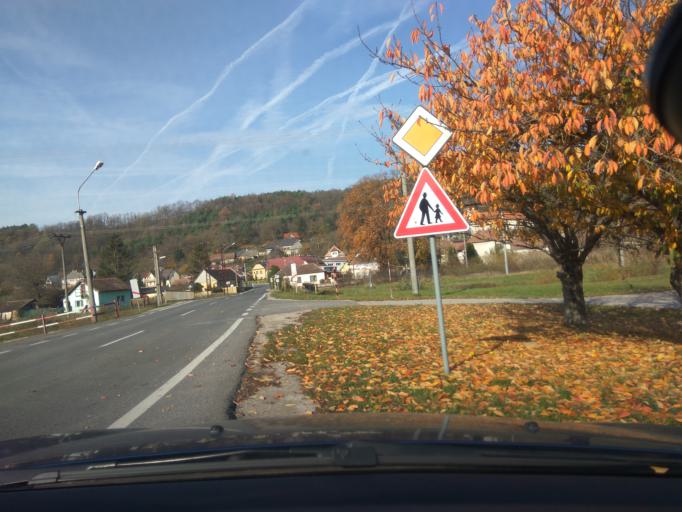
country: SK
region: Nitriansky
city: Brezova pod Bradlom
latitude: 48.6293
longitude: 17.4852
